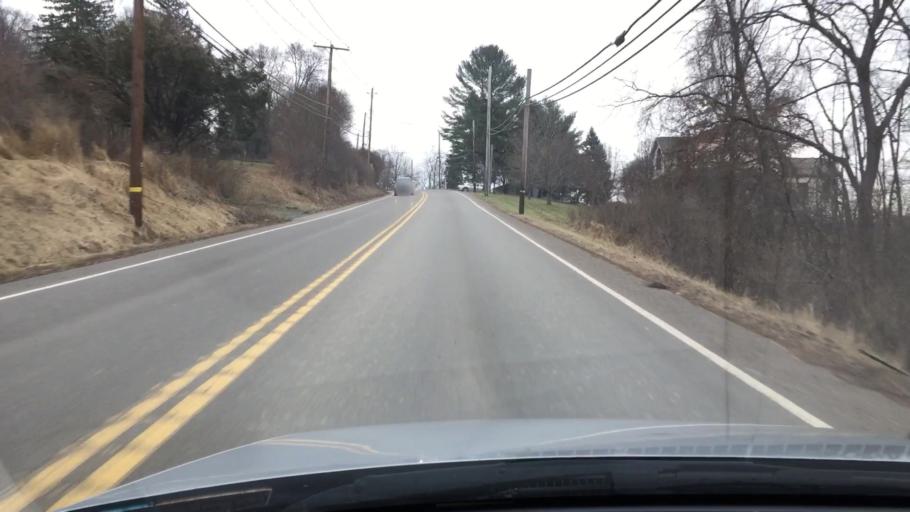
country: US
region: Pennsylvania
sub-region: Columbia County
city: Bloomsburg
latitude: 41.0150
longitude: -76.4407
